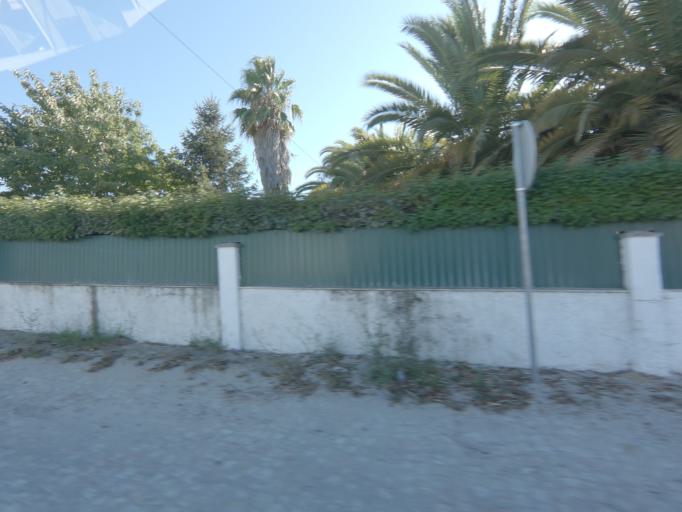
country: PT
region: Setubal
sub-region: Palmela
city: Palmela
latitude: 38.5881
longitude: -8.9181
